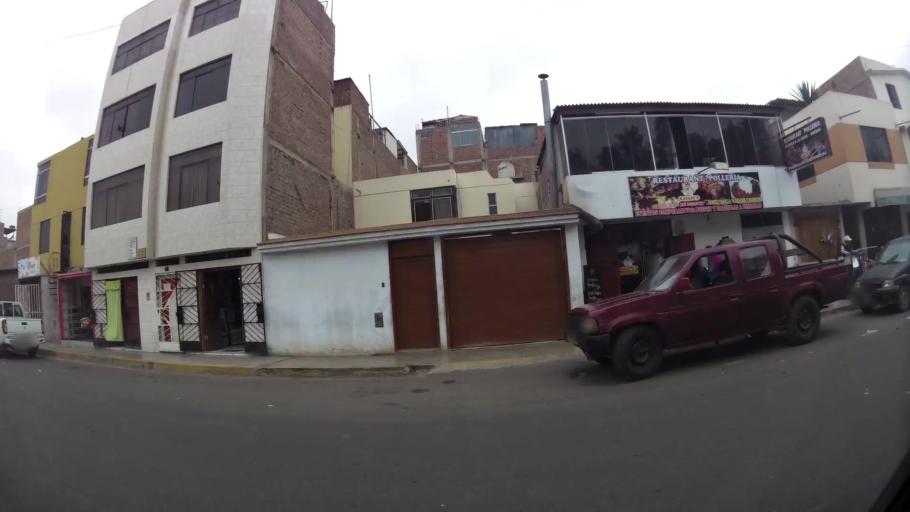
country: PE
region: La Libertad
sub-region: Provincia de Trujillo
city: Trujillo
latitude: -8.1227
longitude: -79.0329
